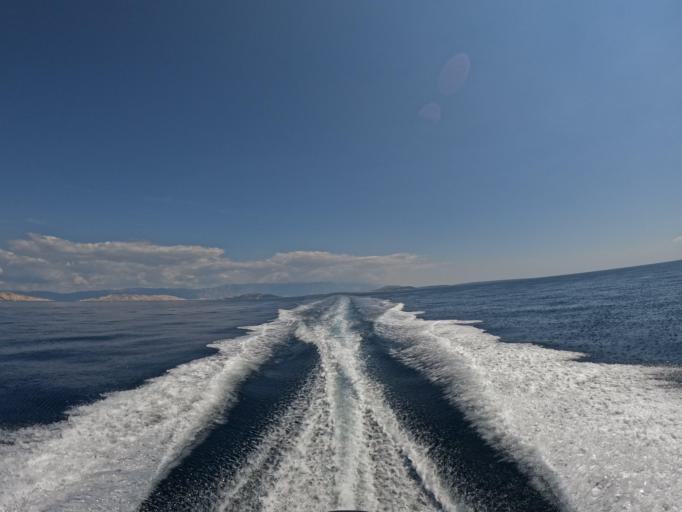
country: HR
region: Primorsko-Goranska
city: Punat
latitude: 44.9069
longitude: 14.5995
